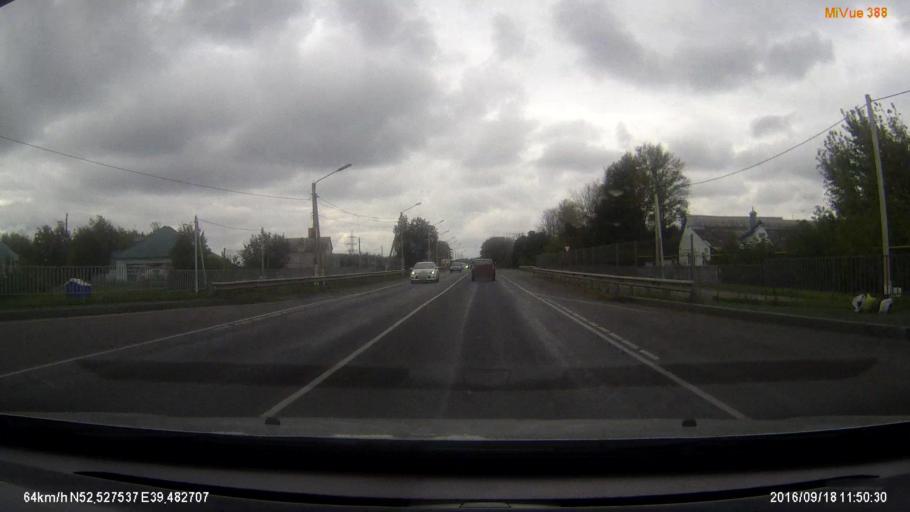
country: RU
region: Lipetsk
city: Syrskoye
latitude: 52.5278
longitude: 39.4831
